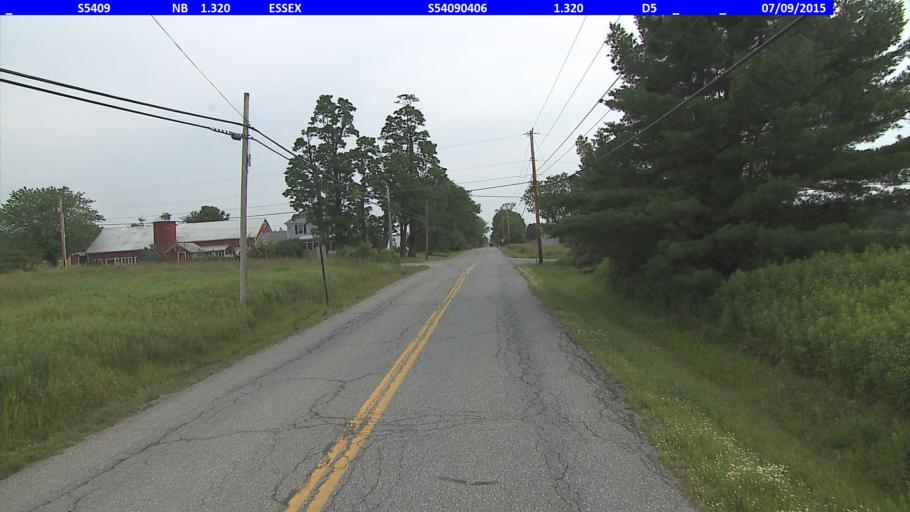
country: US
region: Vermont
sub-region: Chittenden County
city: Essex Junction
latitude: 44.5284
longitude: -73.0774
